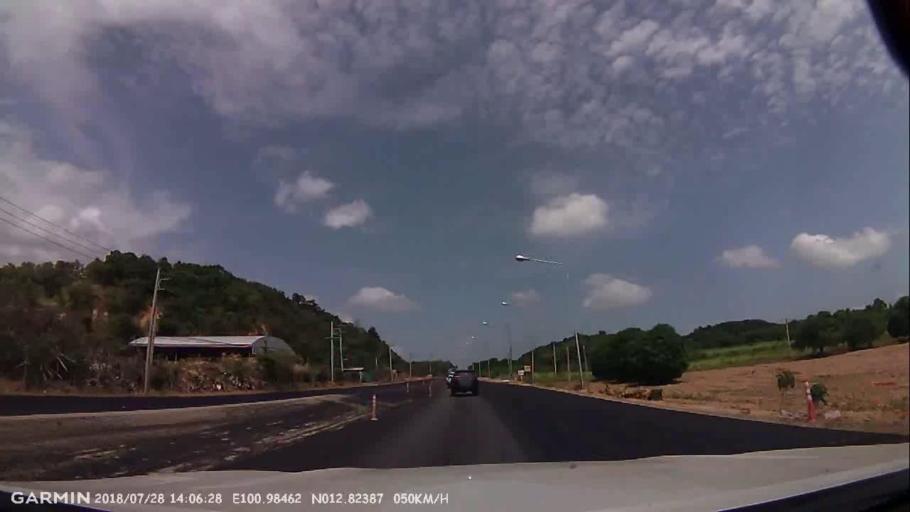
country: TH
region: Rayong
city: Ban Chang
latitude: 12.8238
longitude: 100.9847
